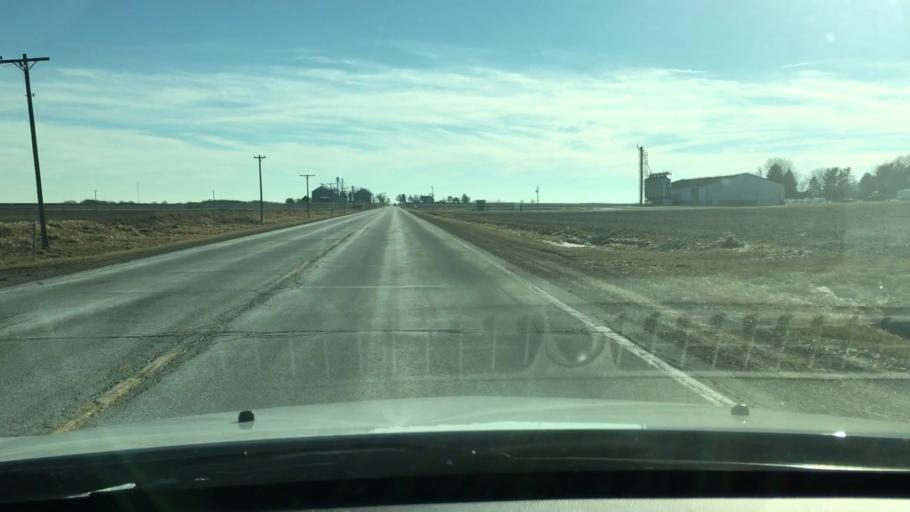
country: US
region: Illinois
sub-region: LaSalle County
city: Mendota
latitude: 41.6024
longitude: -89.1286
